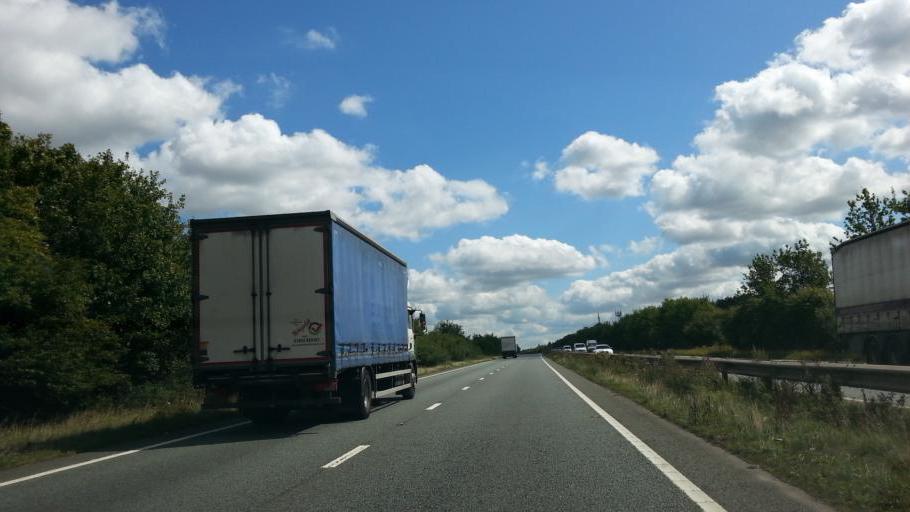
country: GB
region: England
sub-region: Northamptonshire
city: Desborough
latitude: 52.4050
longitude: -0.8728
